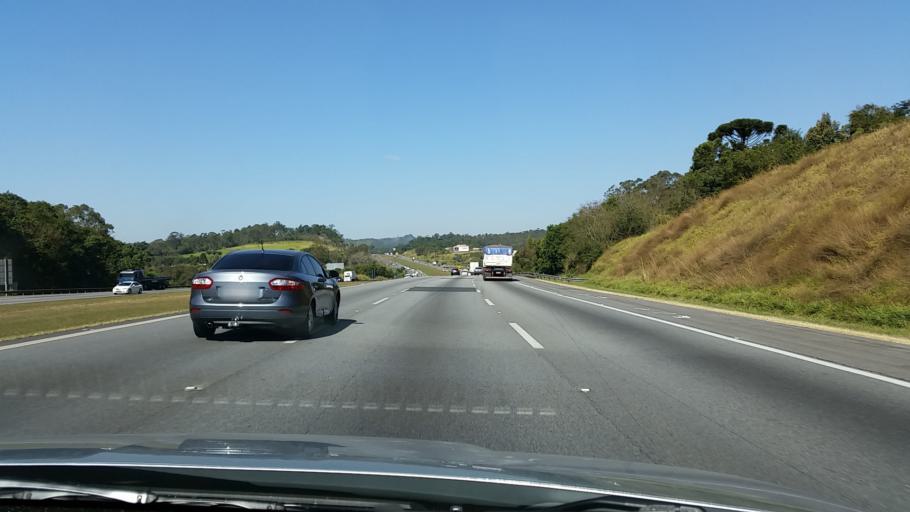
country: BR
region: Sao Paulo
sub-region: Jundiai
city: Jundiai
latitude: -23.2429
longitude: -46.8830
